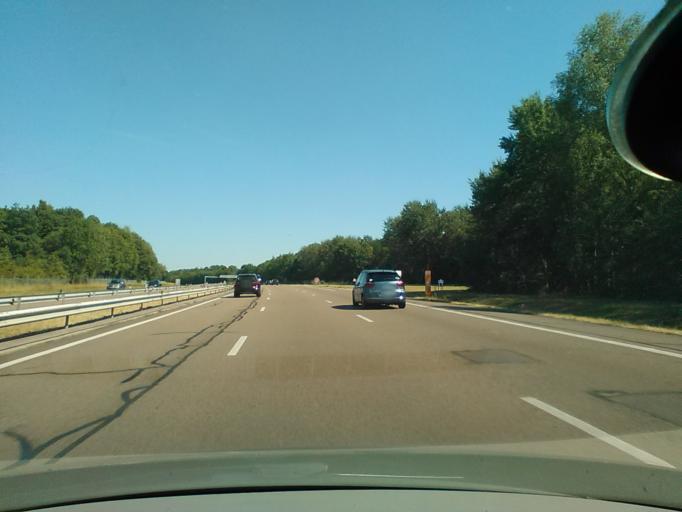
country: FR
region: Bourgogne
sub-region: Departement de l'Yonne
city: Aillant-sur-Tholon
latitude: 47.9121
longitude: 3.2952
